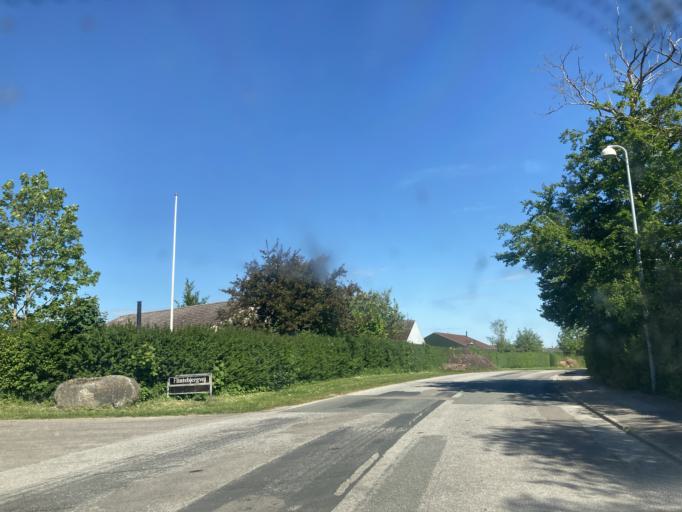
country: DK
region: Zealand
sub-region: Greve Kommune
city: Tune
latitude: 55.6256
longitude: 12.1891
